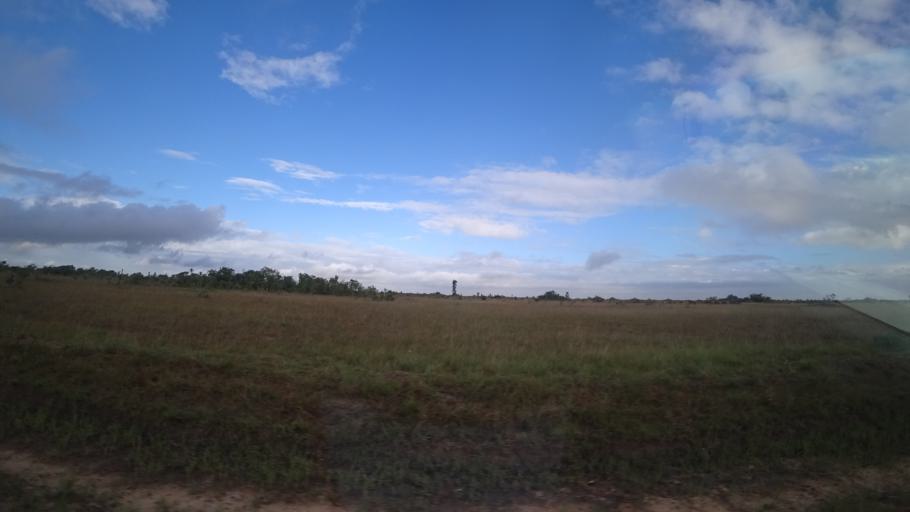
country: MZ
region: Sofala
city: Beira
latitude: -19.6774
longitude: 35.0595
